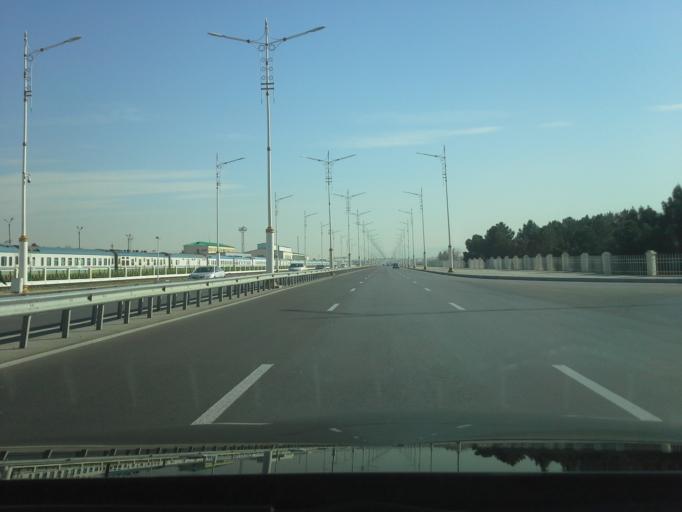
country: TM
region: Ahal
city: Ashgabat
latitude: 37.9369
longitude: 58.4070
